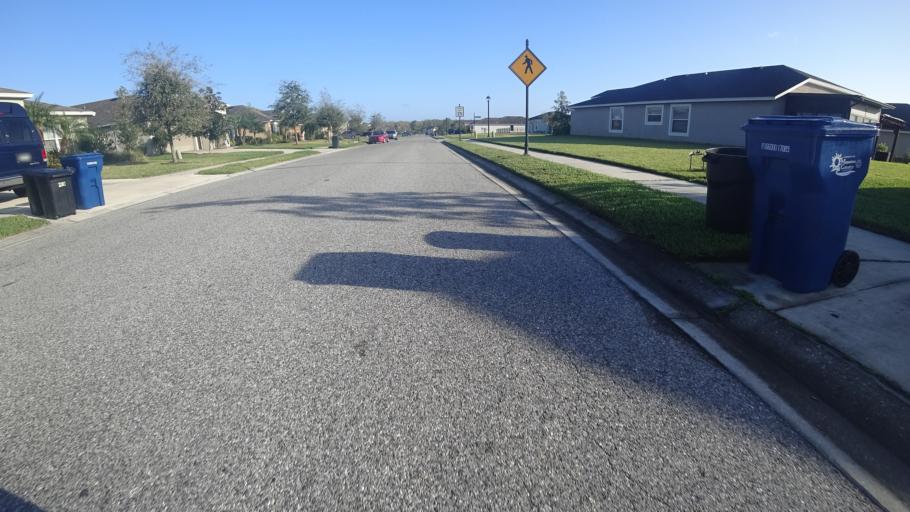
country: US
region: Florida
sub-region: Manatee County
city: Ellenton
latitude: 27.5664
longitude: -82.4560
